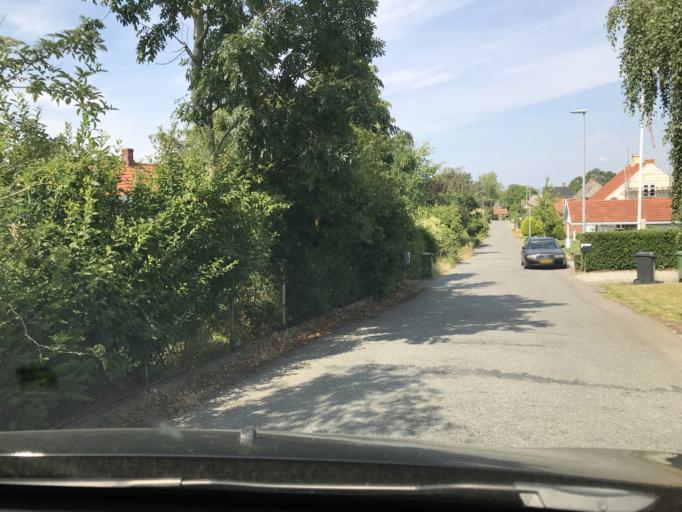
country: DK
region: South Denmark
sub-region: Faaborg-Midtfyn Kommune
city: Faaborg
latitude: 54.9381
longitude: 10.2593
